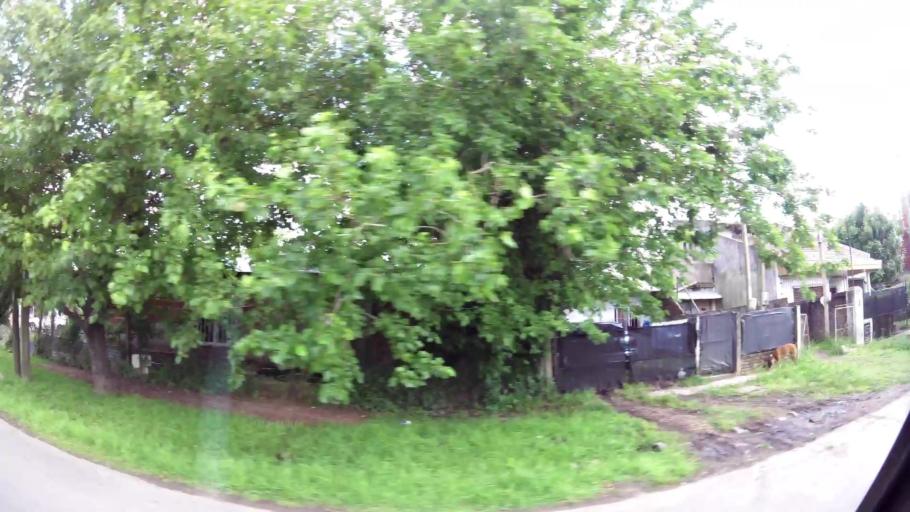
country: AR
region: Buenos Aires
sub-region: Partido de Quilmes
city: Quilmes
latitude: -34.8317
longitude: -58.1736
